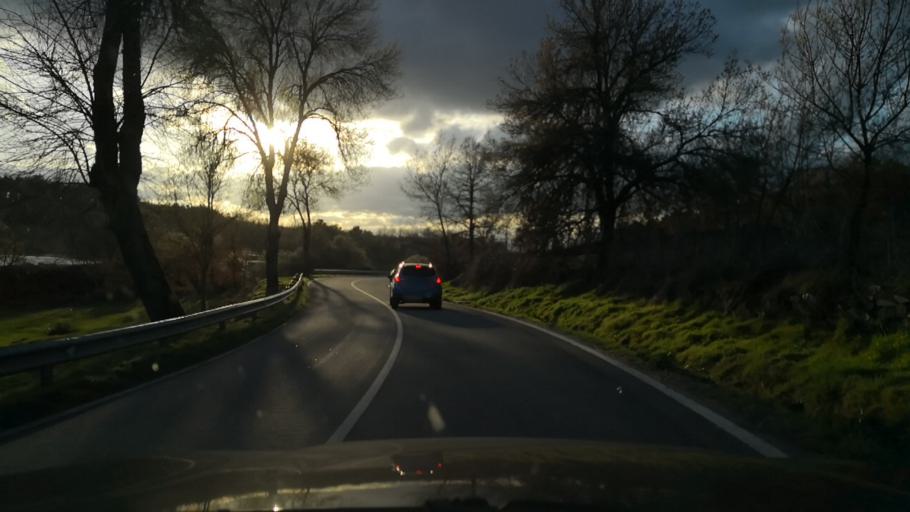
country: PT
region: Braganca
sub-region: Carrazeda de Ansiaes
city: Carrazeda de Anciaes
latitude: 41.2296
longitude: -7.3311
